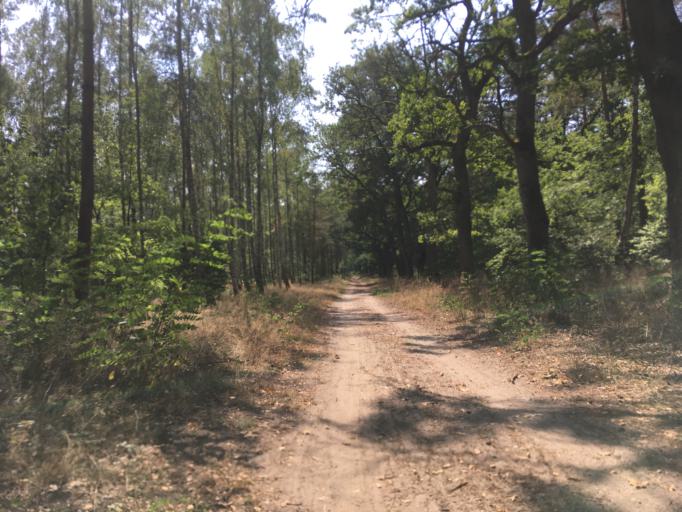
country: DE
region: Berlin
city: Friedrichshagen
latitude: 52.4694
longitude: 13.6062
